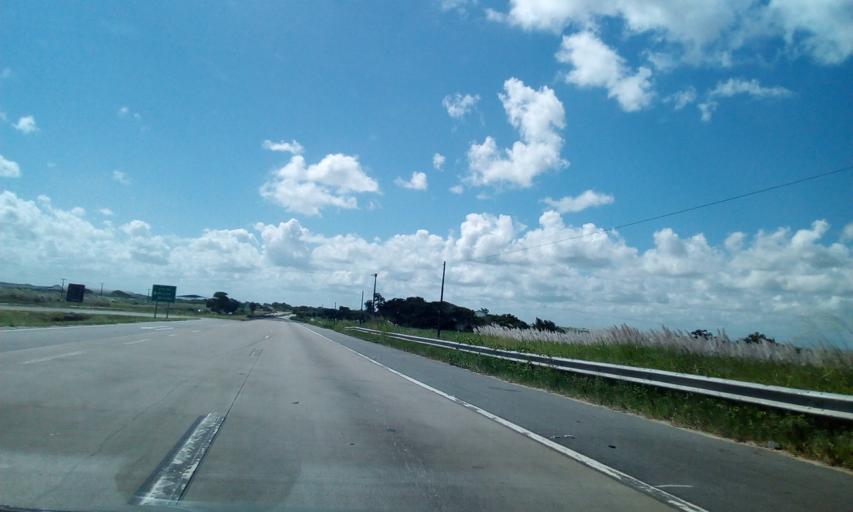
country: BR
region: Pernambuco
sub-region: Itapissuma
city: Itapissuma
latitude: -7.7320
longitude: -34.9412
